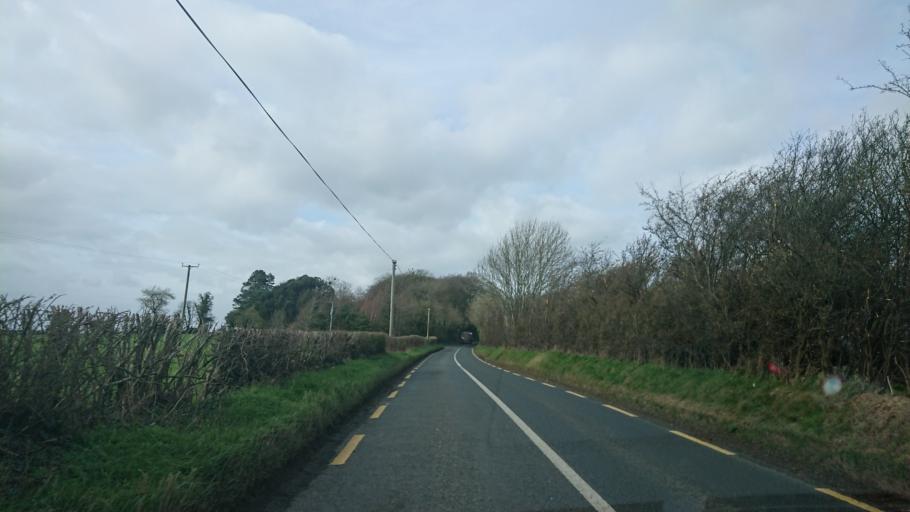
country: IE
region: Leinster
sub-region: Kildare
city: Naas
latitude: 53.1741
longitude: -6.6359
